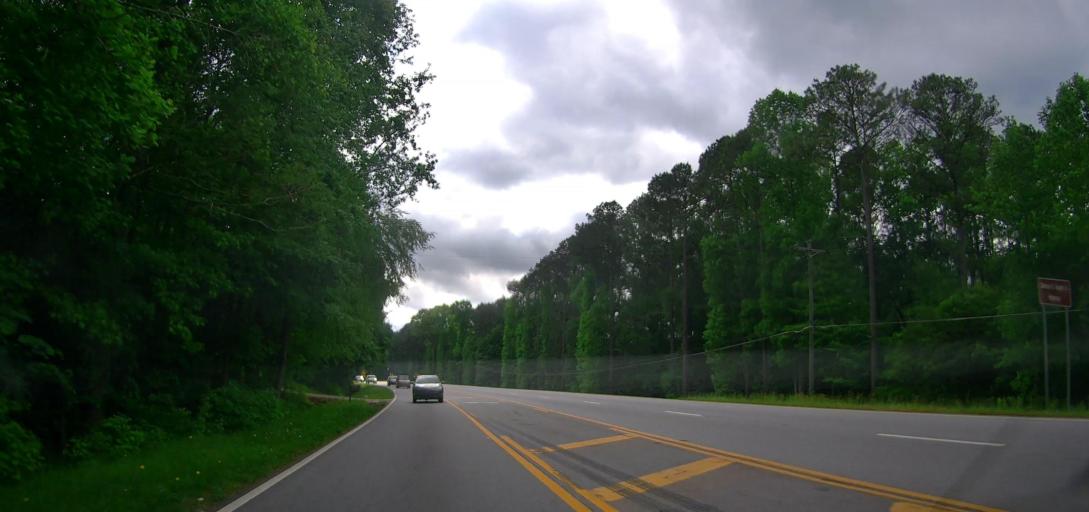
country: US
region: Georgia
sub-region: Walton County
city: Walnut Grove
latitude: 33.7212
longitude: -83.9221
